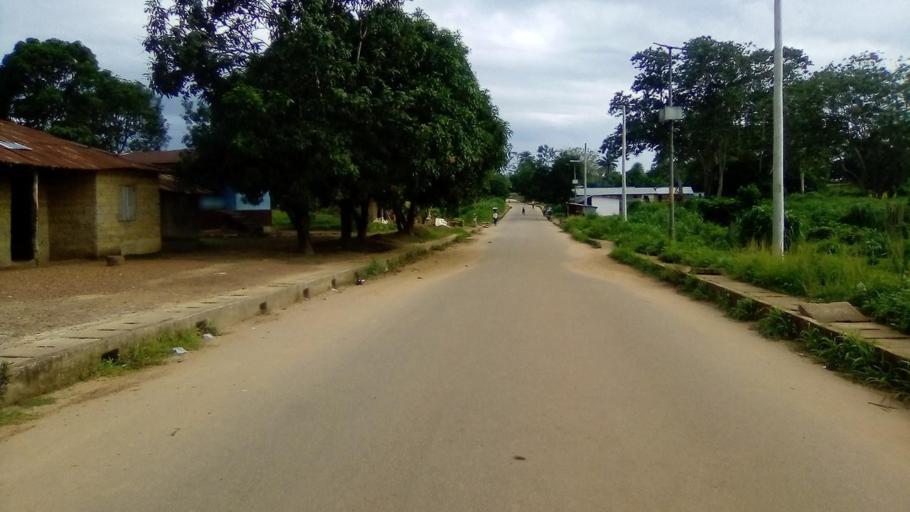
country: SL
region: Southern Province
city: Pujehun
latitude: 7.3642
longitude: -11.7248
